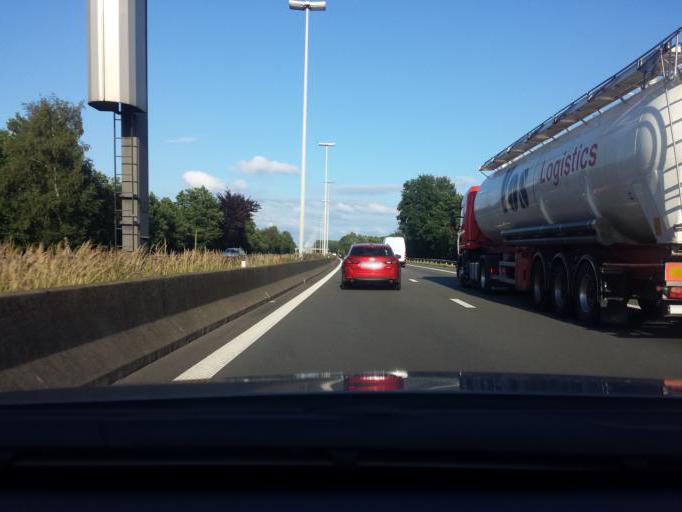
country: BE
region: Flanders
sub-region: Provincie Antwerpen
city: Nijlen
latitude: 51.1818
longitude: 4.6861
